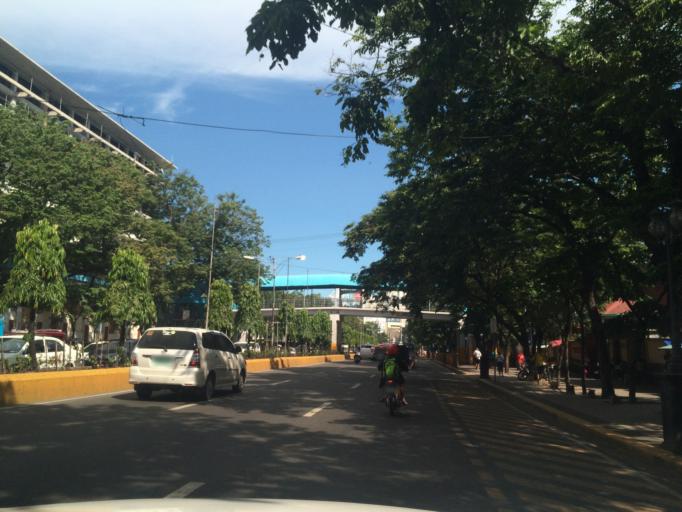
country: PH
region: Central Visayas
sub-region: Cebu City
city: Calero
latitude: 10.3016
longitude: 123.8960
